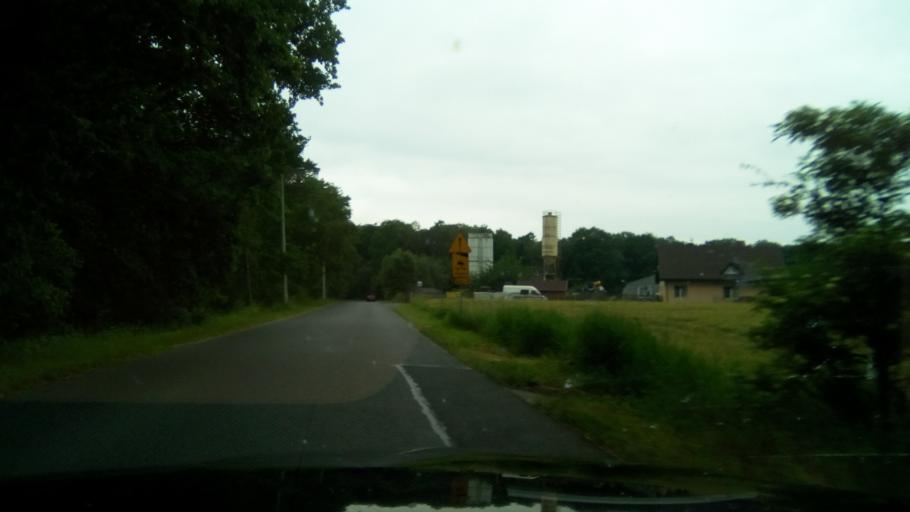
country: PL
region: Greater Poland Voivodeship
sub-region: Powiat gnieznienski
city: Czerniejewo
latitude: 52.4712
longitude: 17.5089
